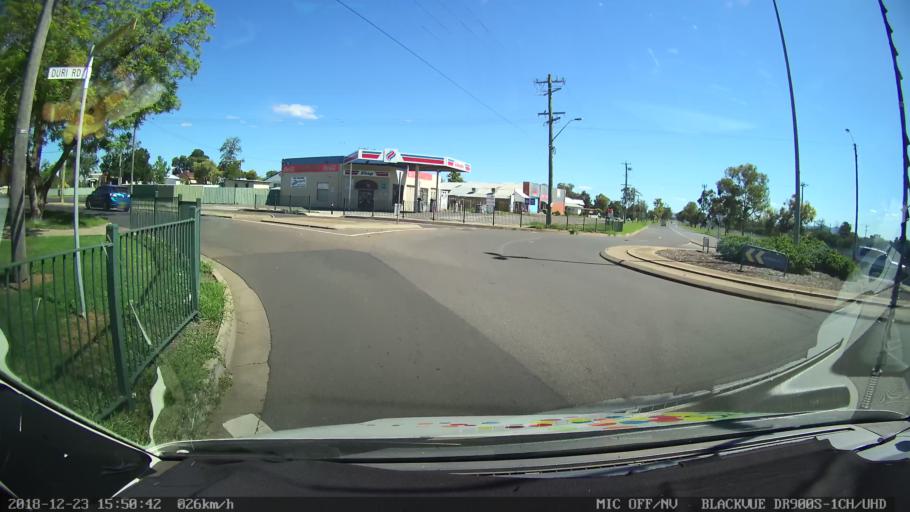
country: AU
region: New South Wales
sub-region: Tamworth Municipality
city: South Tamworth
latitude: -31.1077
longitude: 150.8996
